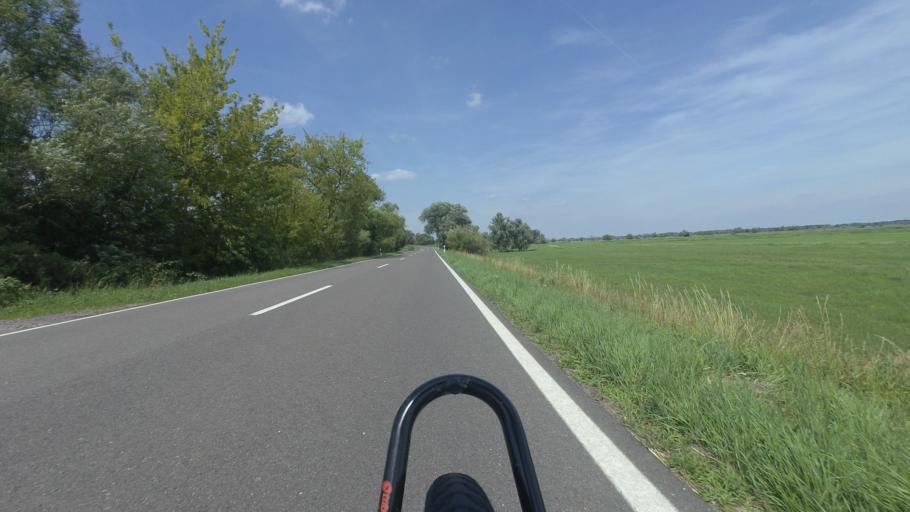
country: DE
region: Saxony-Anhalt
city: Schollene
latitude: 52.7670
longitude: 12.2250
